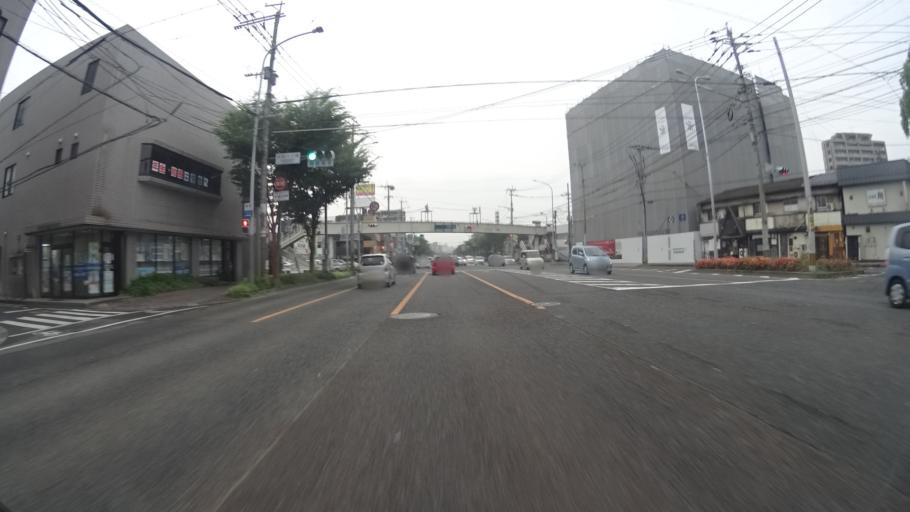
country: JP
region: Fukuoka
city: Onojo
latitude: 33.5482
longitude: 130.4424
